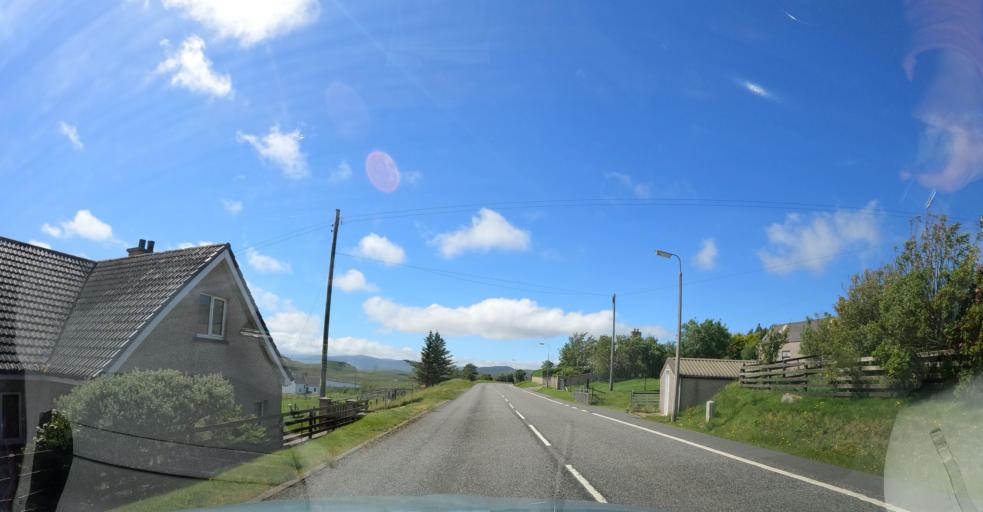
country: GB
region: Scotland
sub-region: Eilean Siar
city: Stornoway
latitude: 58.0901
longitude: -6.6156
